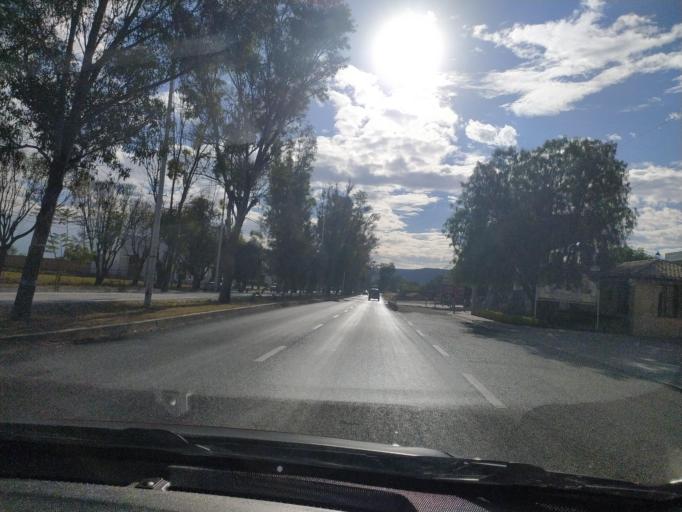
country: LA
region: Oudomxai
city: Muang La
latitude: 21.0305
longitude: 101.8439
